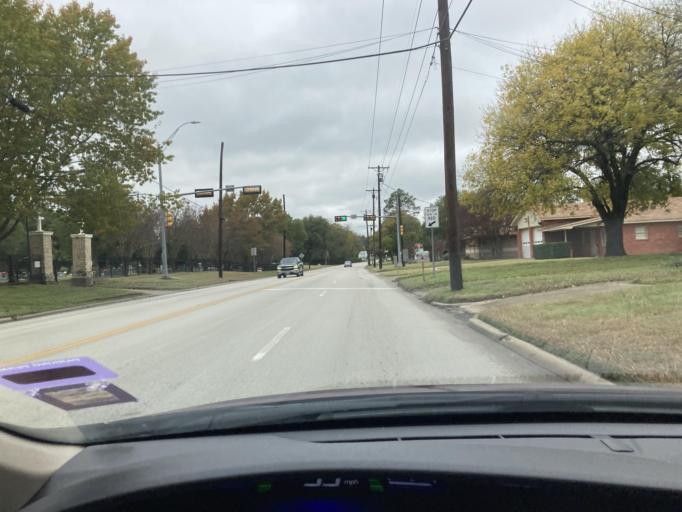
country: US
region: Texas
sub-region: Navarro County
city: Corsicana
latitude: 32.0861
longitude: -96.4889
